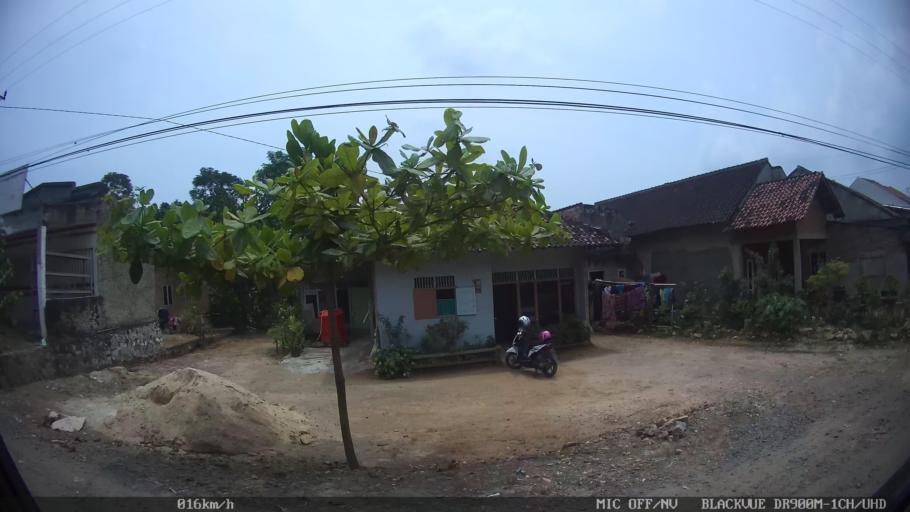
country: ID
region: Lampung
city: Kedaton
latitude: -5.3945
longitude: 105.3173
